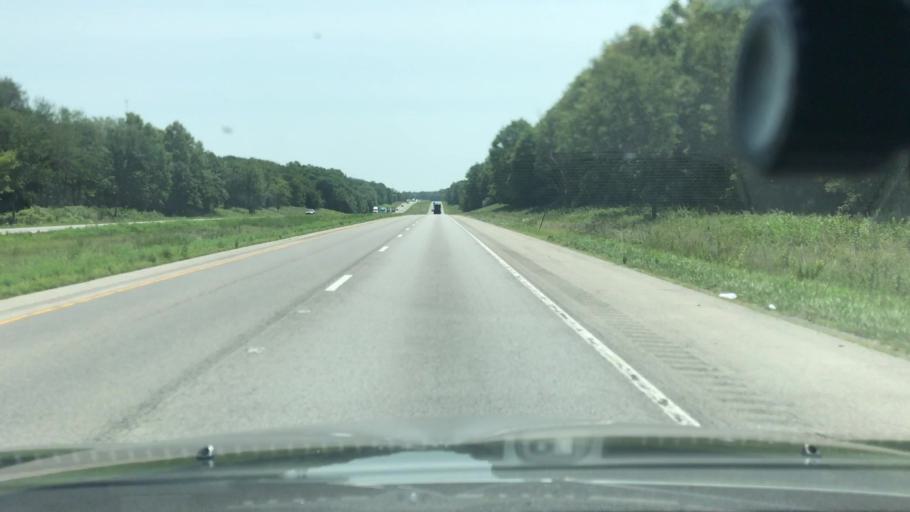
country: US
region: Illinois
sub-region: Clinton County
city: Wamac
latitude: 38.3732
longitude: -89.0995
